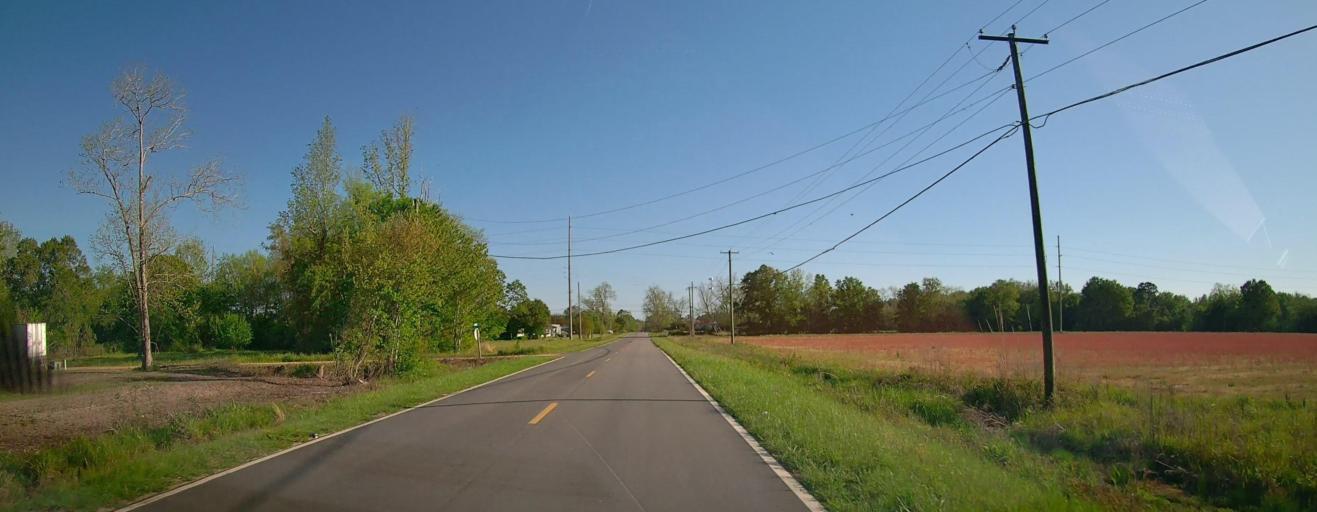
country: US
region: Georgia
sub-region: Ben Hill County
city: Fitzgerald
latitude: 31.7359
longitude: -83.2802
